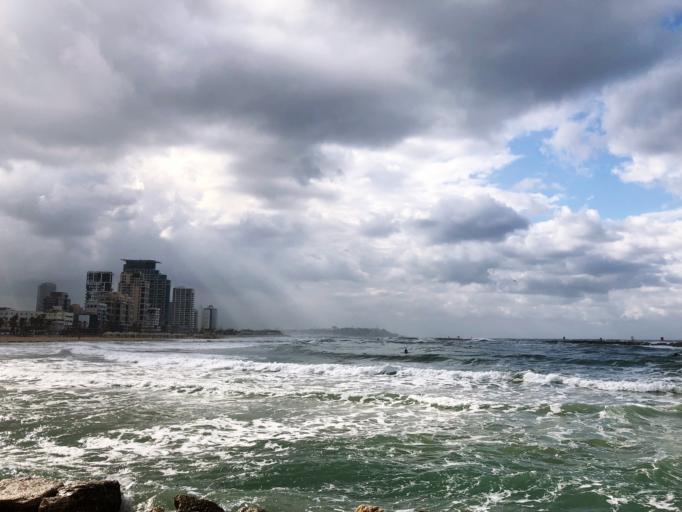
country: IL
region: Tel Aviv
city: Tel Aviv
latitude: 32.0775
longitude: 34.7647
